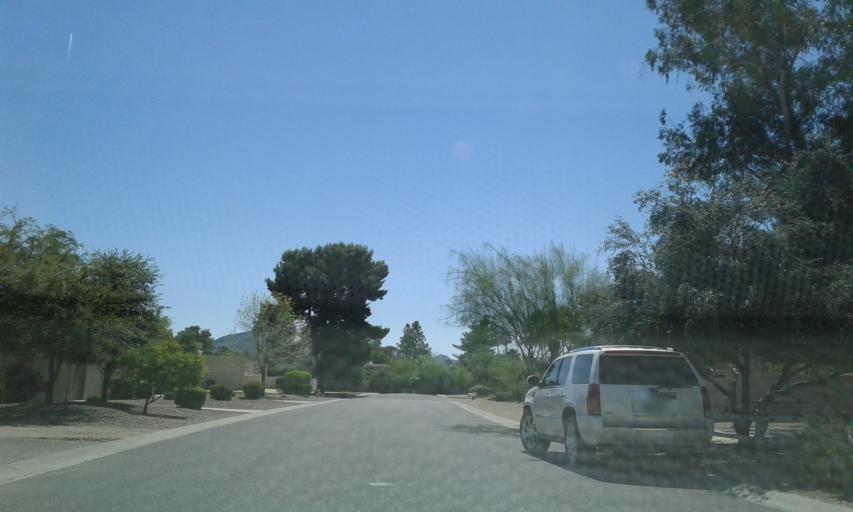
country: US
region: Arizona
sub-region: Maricopa County
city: Paradise Valley
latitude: 33.5876
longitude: -111.9676
